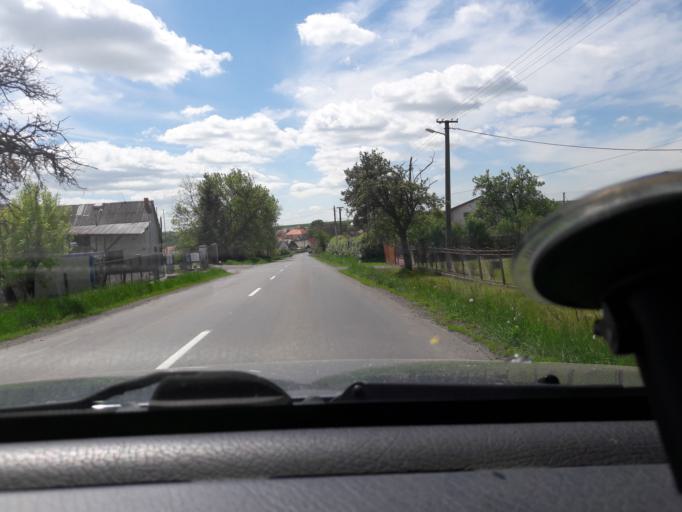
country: SK
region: Banskobystricky
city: Dudince
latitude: 48.2763
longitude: 18.9572
